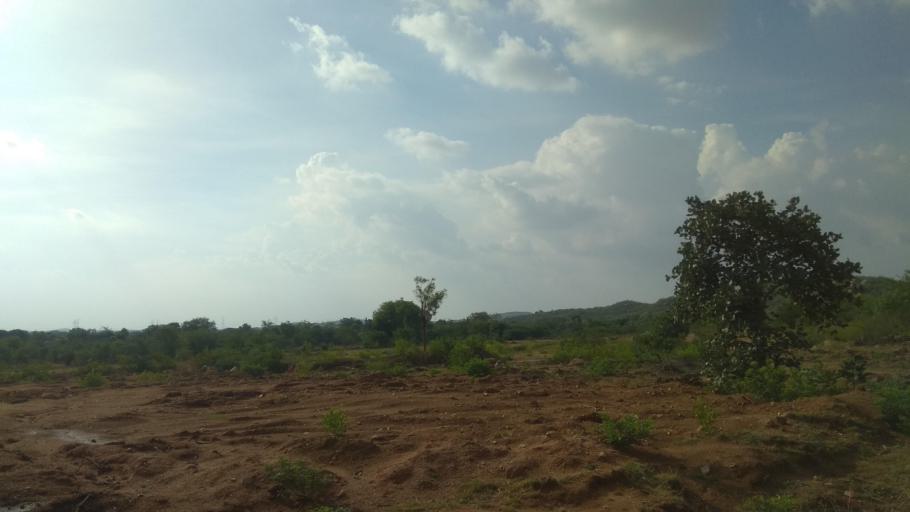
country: IN
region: Telangana
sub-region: Mahbubnagar
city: Farrukhnagar
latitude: 16.8894
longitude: 78.4800
